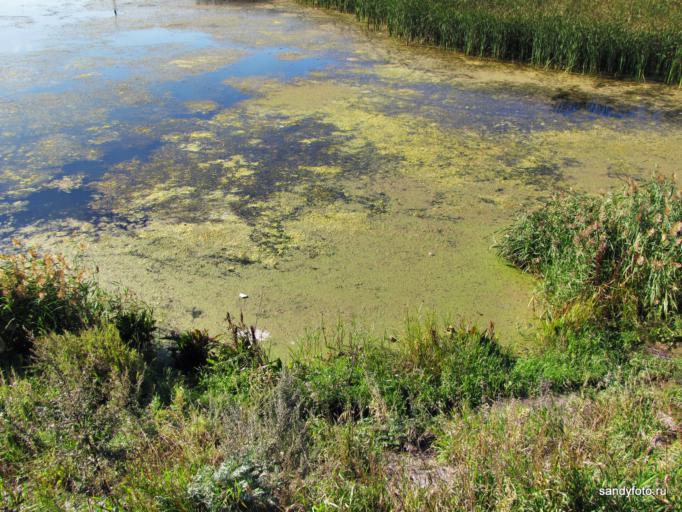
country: RU
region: Chelyabinsk
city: Troitsk
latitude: 54.0921
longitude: 61.5764
